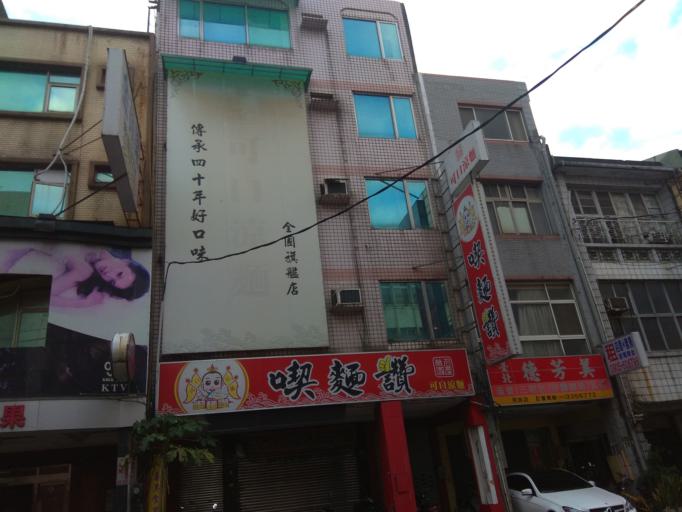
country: TW
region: Taiwan
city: Taoyuan City
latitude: 24.9948
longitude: 121.3077
